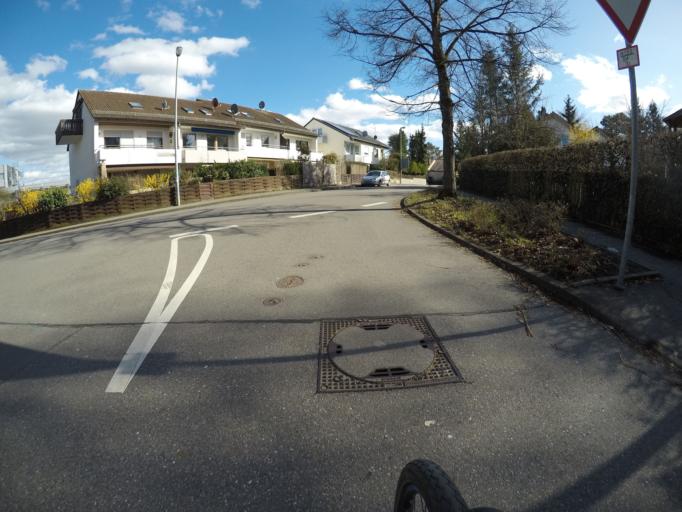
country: DE
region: Baden-Wuerttemberg
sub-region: Regierungsbezirk Stuttgart
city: Filderstadt
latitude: 48.6549
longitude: 9.2008
